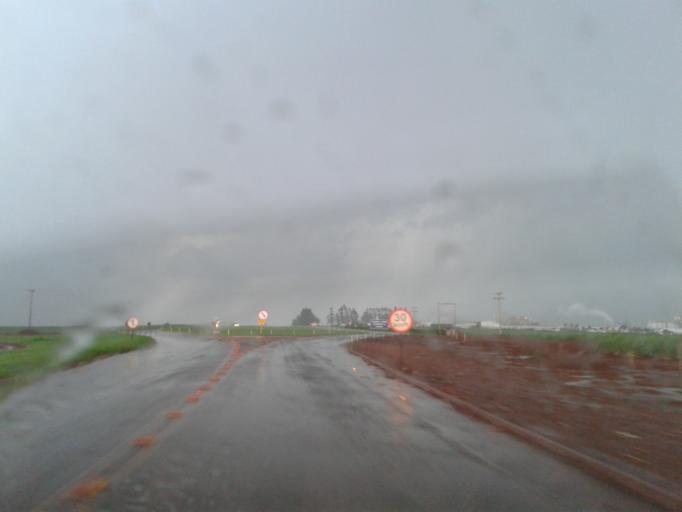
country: BR
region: Goias
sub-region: Quirinopolis
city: Quirinopolis
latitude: -18.5586
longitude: -50.4396
